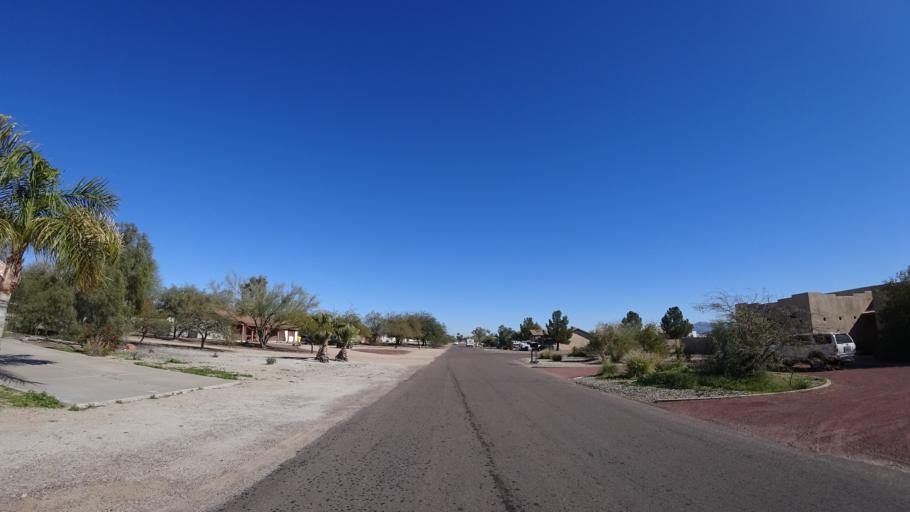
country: US
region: Arizona
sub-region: Maricopa County
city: Buckeye
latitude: 33.4276
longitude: -112.5366
